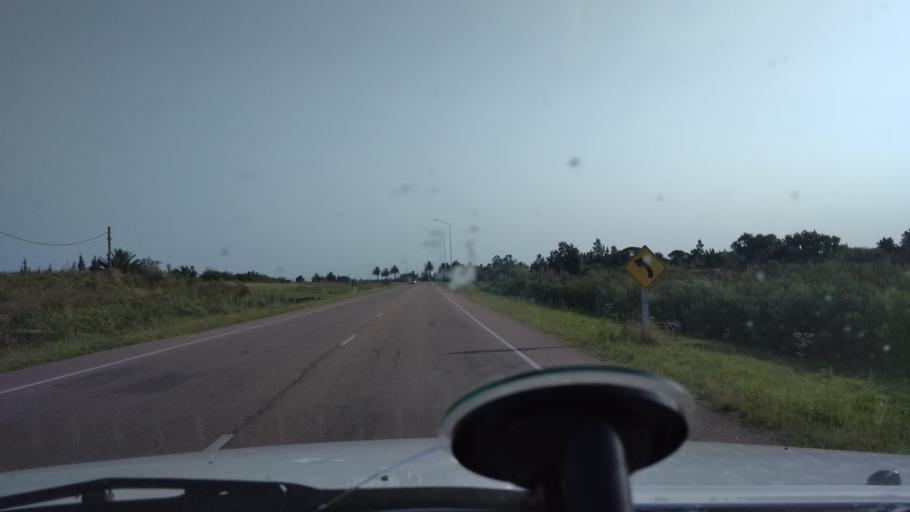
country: UY
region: Canelones
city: Sauce
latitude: -34.6603
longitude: -56.0564
